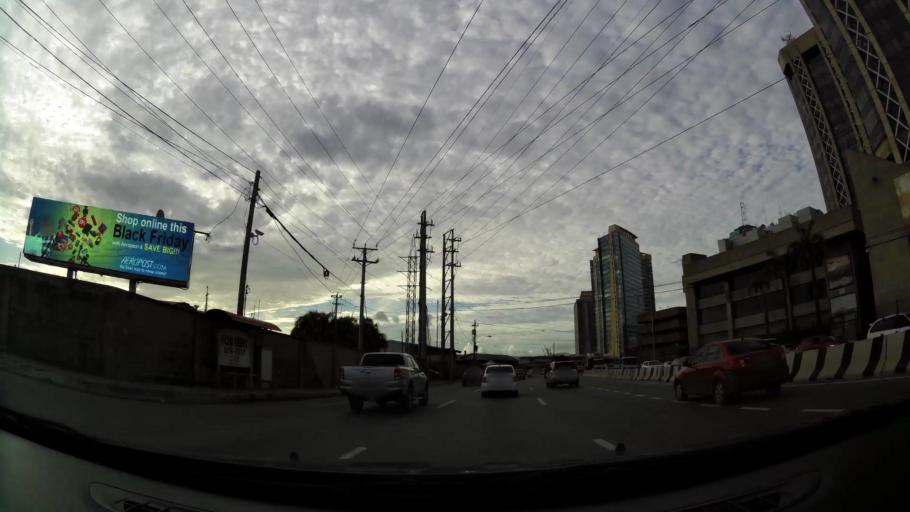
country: TT
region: San Juan/Laventille
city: Laventille
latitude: 10.6479
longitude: -61.5123
